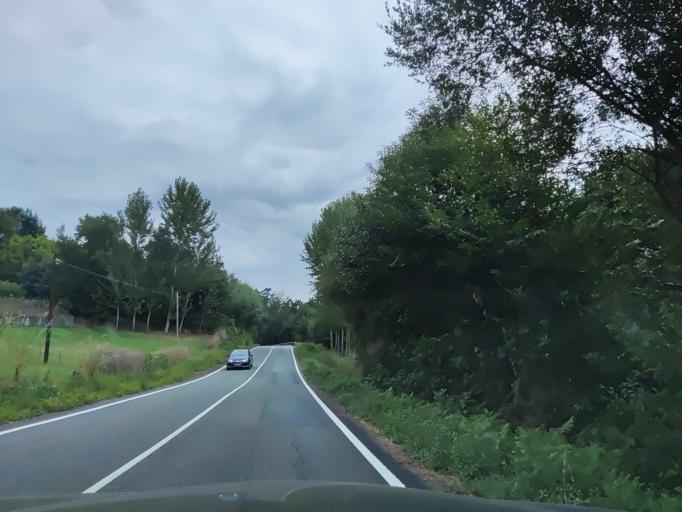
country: ES
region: Galicia
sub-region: Provincia da Coruna
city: Teo
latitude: 42.7567
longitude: -8.5610
